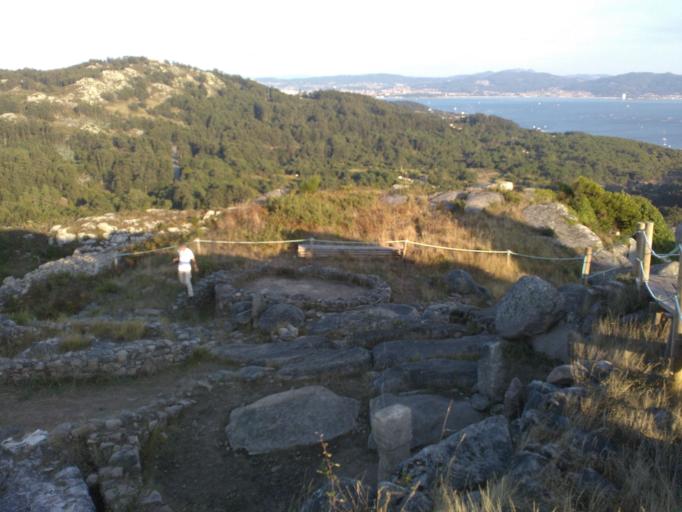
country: ES
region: Galicia
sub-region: Provincia de Pontevedra
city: Cangas
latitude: 42.2766
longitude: -8.8610
